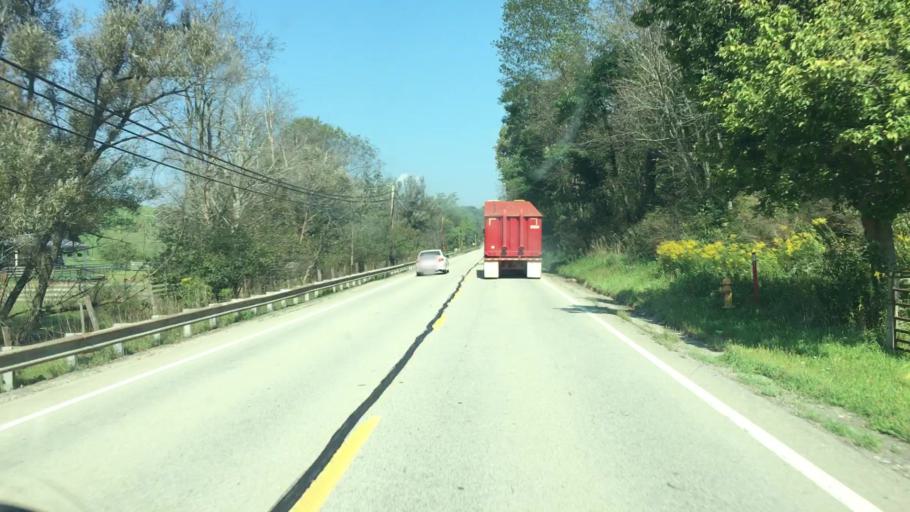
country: US
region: Pennsylvania
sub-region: Washington County
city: Washington
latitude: 40.0657
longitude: -80.2977
